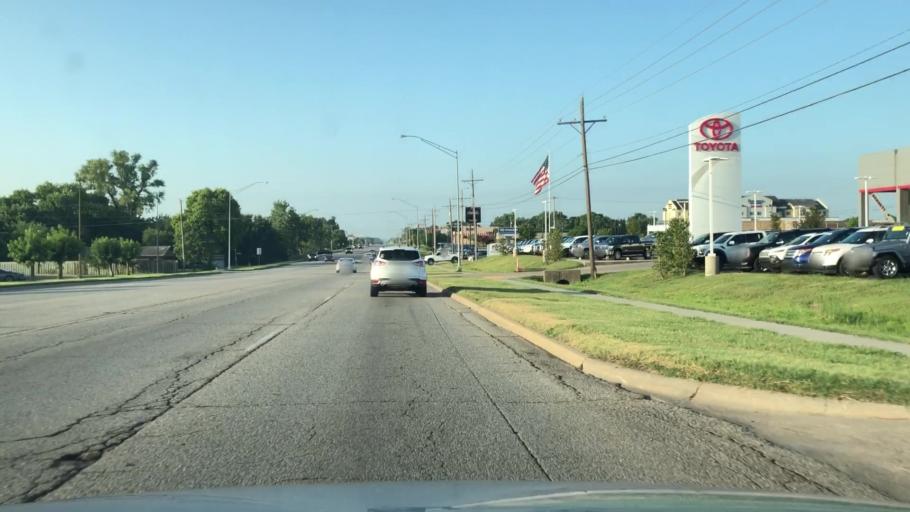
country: US
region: Oklahoma
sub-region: Washington County
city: Bartlesville
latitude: 36.7236
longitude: -95.9352
